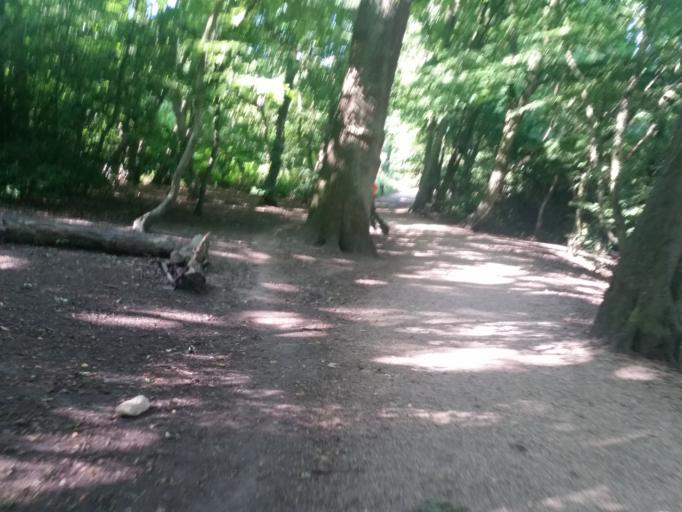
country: GB
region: England
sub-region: Greater London
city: Crouch End
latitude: 51.5804
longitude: -0.1475
